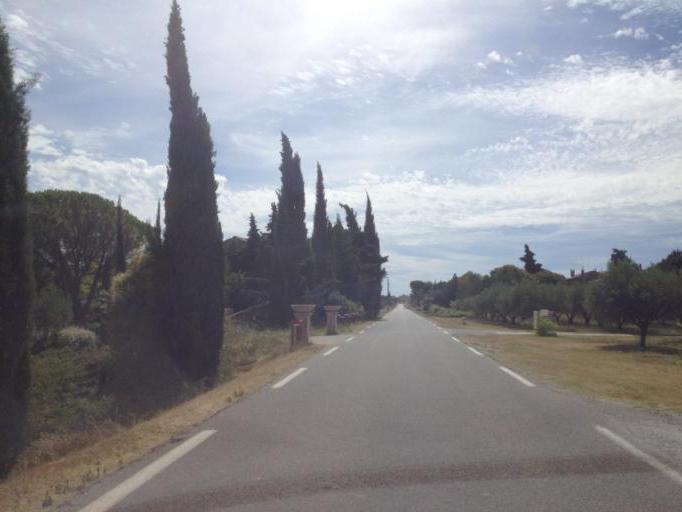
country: FR
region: Provence-Alpes-Cote d'Azur
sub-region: Departement du Vaucluse
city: Caromb
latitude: 44.1218
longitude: 5.0725
